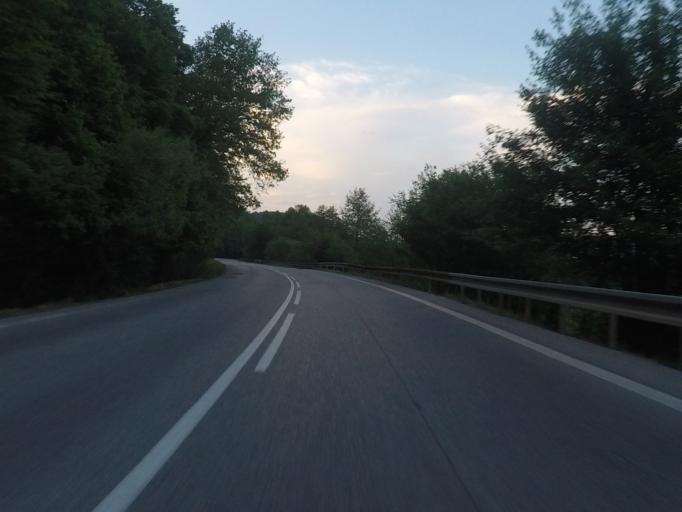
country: SK
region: Banskobystricky
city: Rimavska Sobota
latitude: 48.5186
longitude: 19.9442
